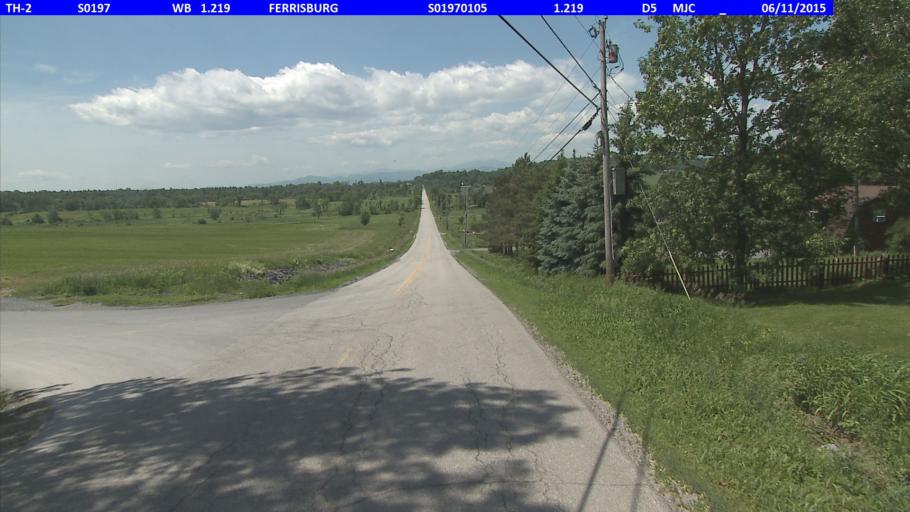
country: US
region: Vermont
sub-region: Addison County
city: Vergennes
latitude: 44.1747
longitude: -73.2152
